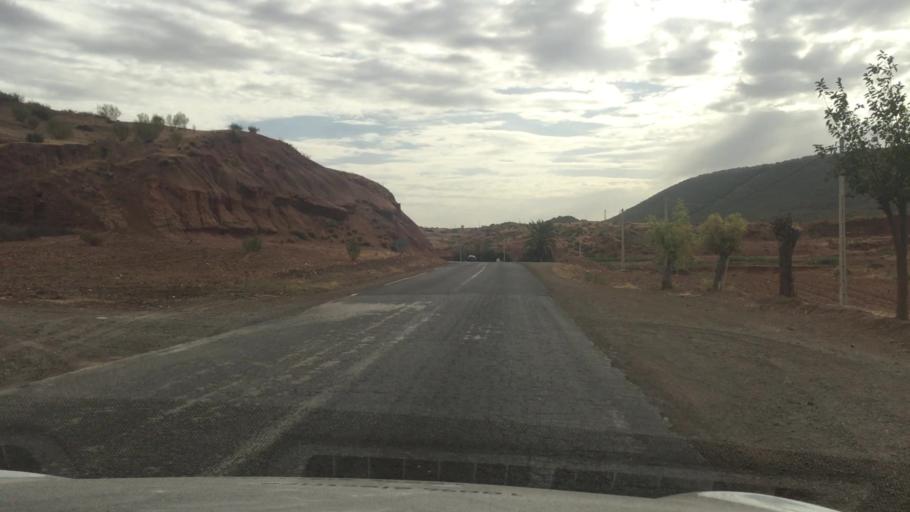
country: MA
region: Marrakech-Tensift-Al Haouz
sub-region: Al-Haouz
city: Touama
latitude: 31.5455
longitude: -7.5704
